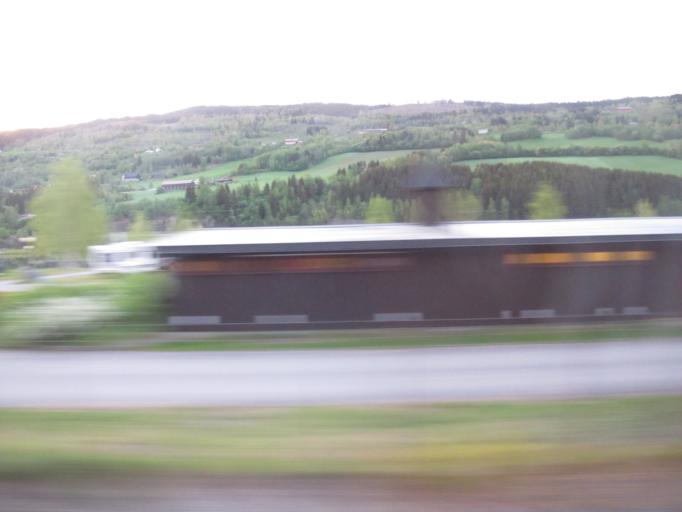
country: NO
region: Oppland
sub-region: Lillehammer
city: Lillehammer
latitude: 61.2241
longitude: 10.4388
